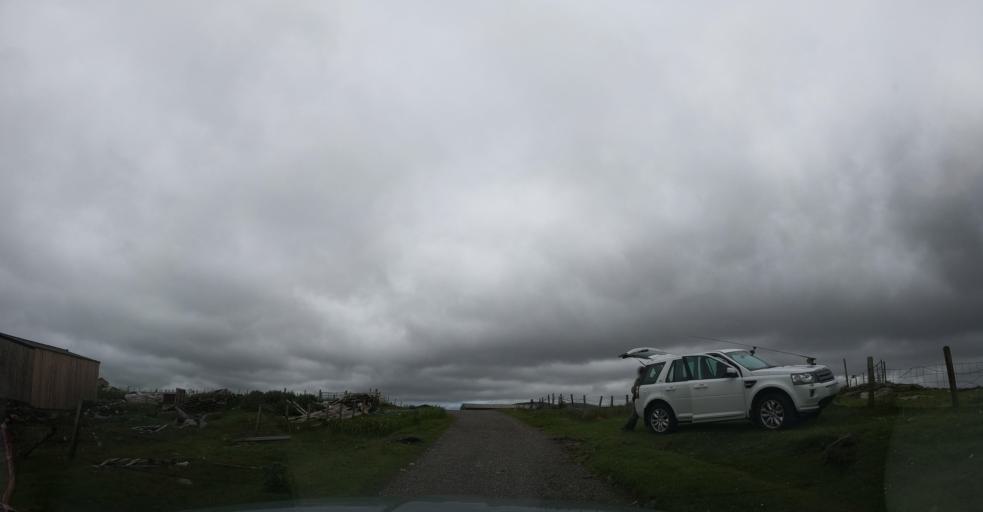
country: GB
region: Scotland
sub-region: Eilean Siar
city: Isle of North Uist
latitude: 57.5467
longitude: -7.3449
